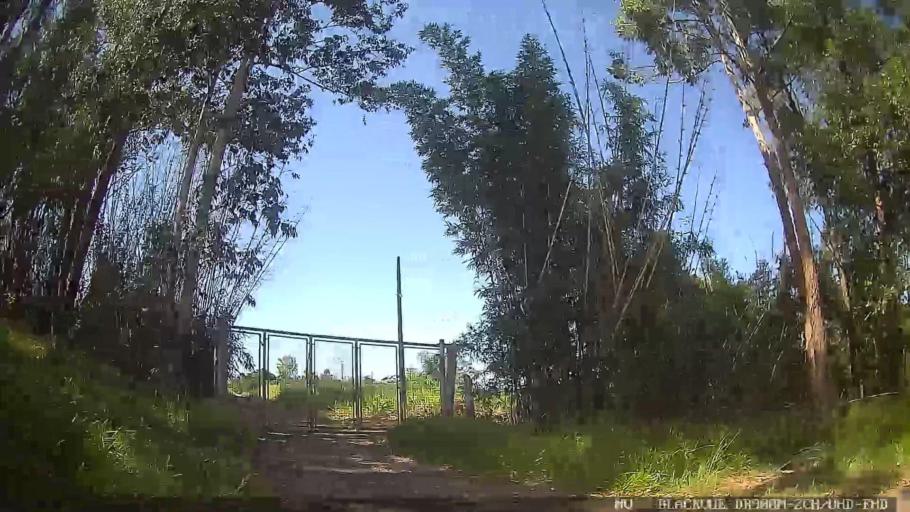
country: BR
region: Sao Paulo
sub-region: Atibaia
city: Atibaia
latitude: -23.1022
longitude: -46.5940
